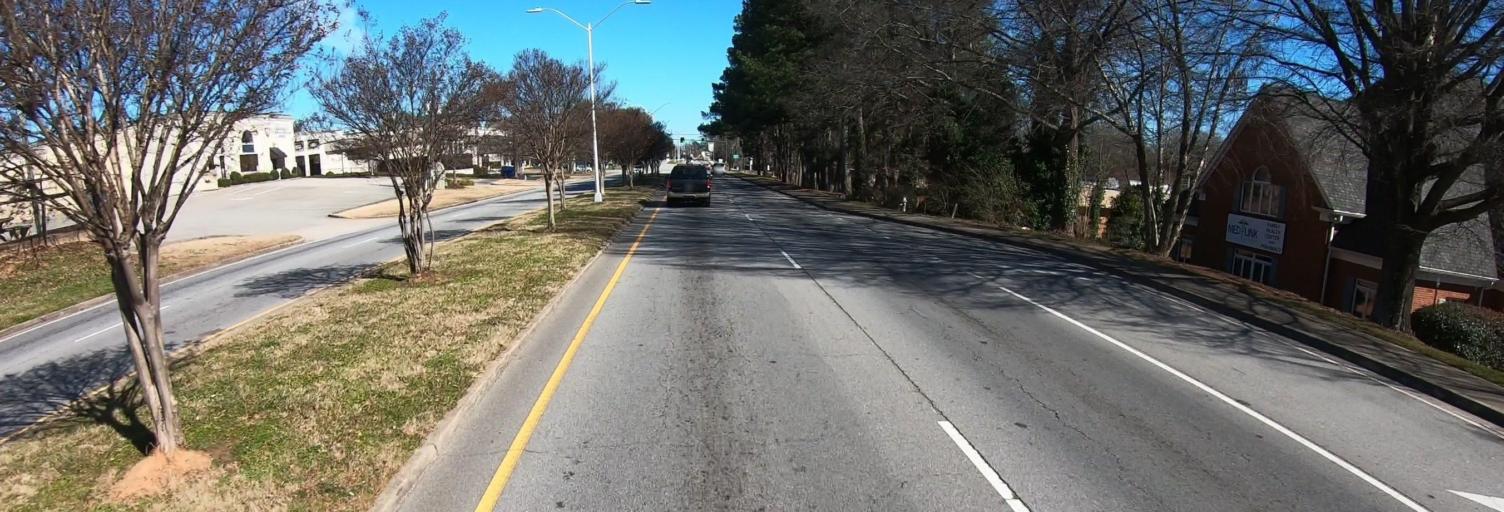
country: US
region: Georgia
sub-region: Hall County
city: Gainesville
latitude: 34.2995
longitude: -83.8210
